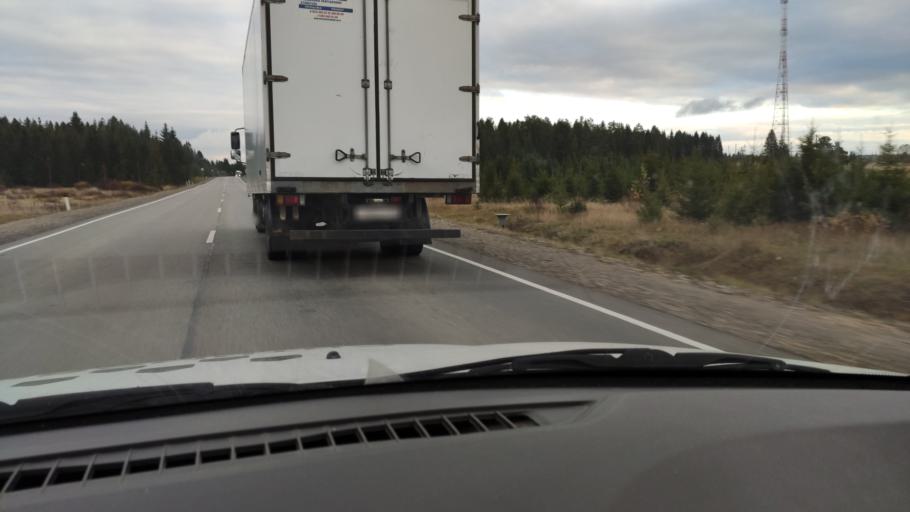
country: RU
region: Kirov
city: Chernaya Kholunitsa
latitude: 58.8547
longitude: 51.7292
